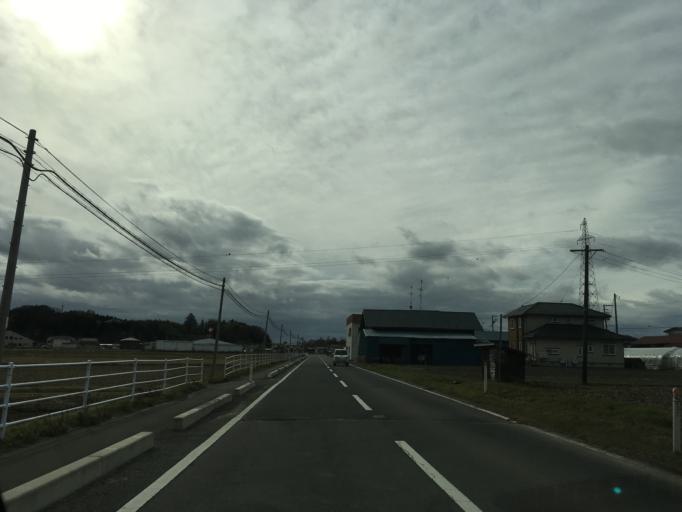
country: JP
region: Iwate
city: Ichinoseki
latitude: 38.7362
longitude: 141.2768
